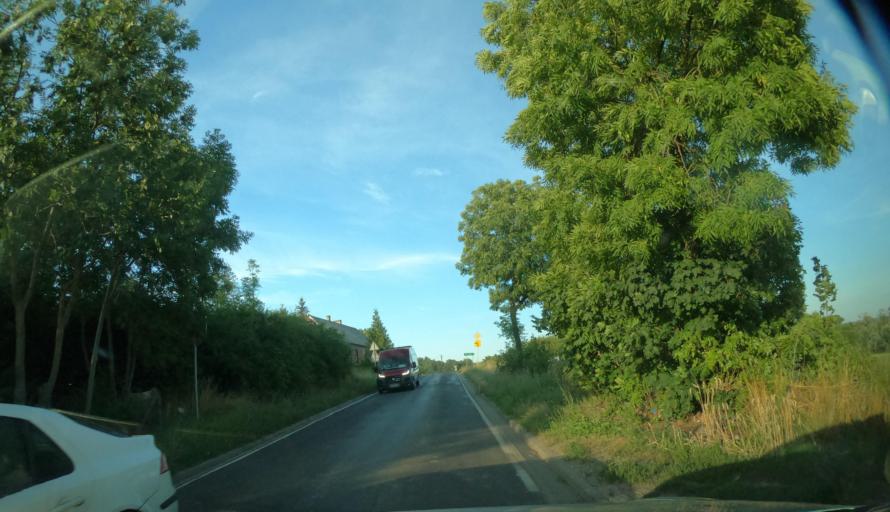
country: PL
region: Kujawsko-Pomorskie
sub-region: Bydgoszcz
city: Fordon
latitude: 53.2326
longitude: 18.2154
